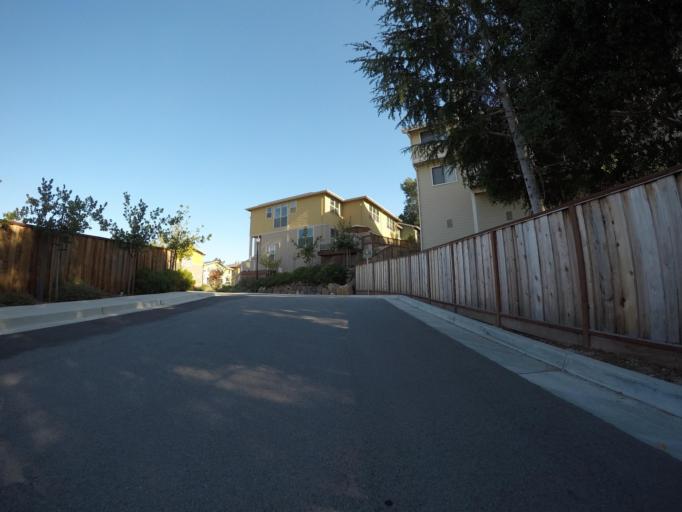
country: US
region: California
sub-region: Santa Cruz County
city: Scotts Valley
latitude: 37.0406
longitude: -122.0263
